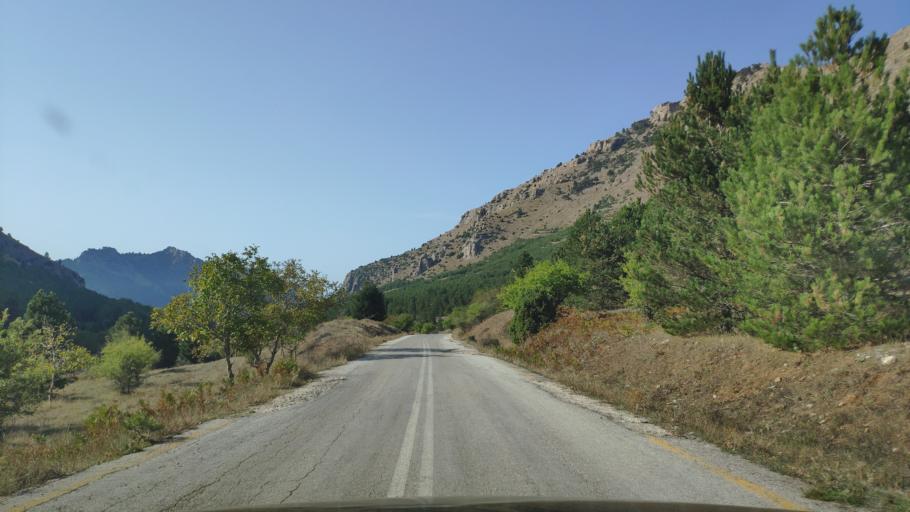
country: GR
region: West Greece
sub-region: Nomos Achaias
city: Aiyira
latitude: 38.0378
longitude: 22.3977
